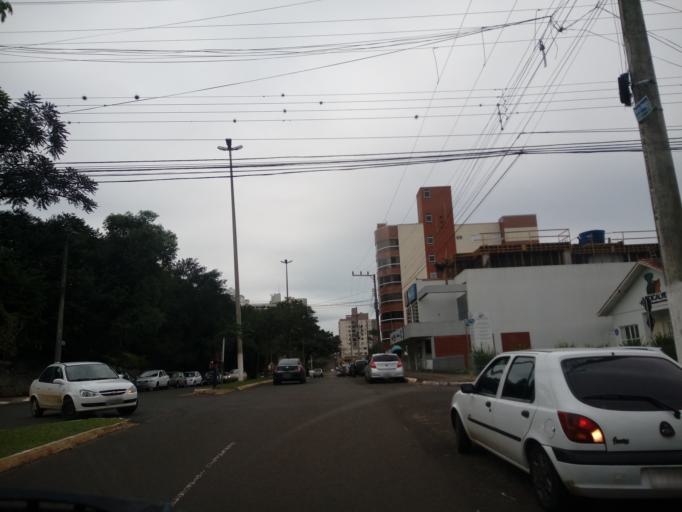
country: BR
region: Santa Catarina
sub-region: Chapeco
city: Chapeco
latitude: -27.0938
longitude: -52.6210
